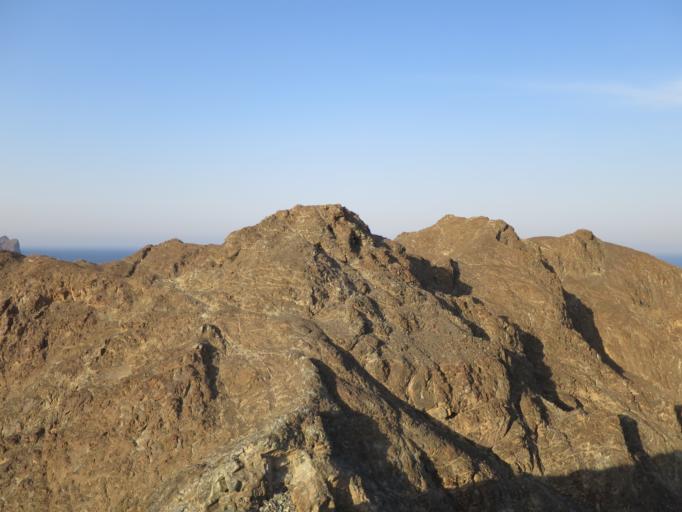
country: OM
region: Muhafazat Masqat
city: Muscat
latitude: 23.5889
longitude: 58.6034
